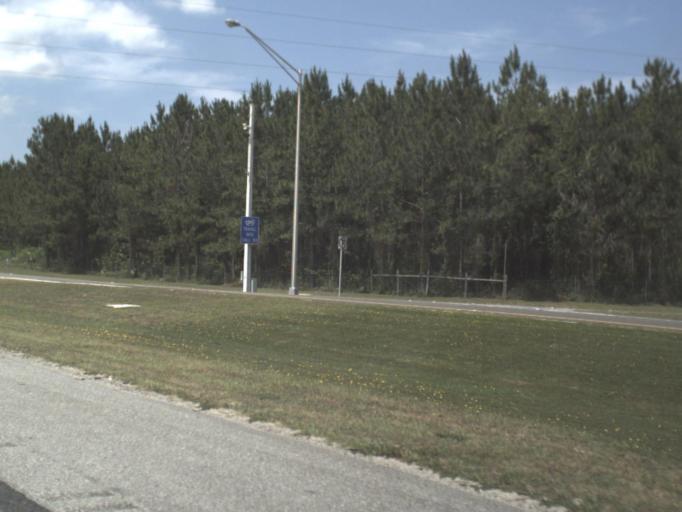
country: US
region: Florida
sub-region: Saint Johns County
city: Palm Valley
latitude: 30.0927
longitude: -81.4977
